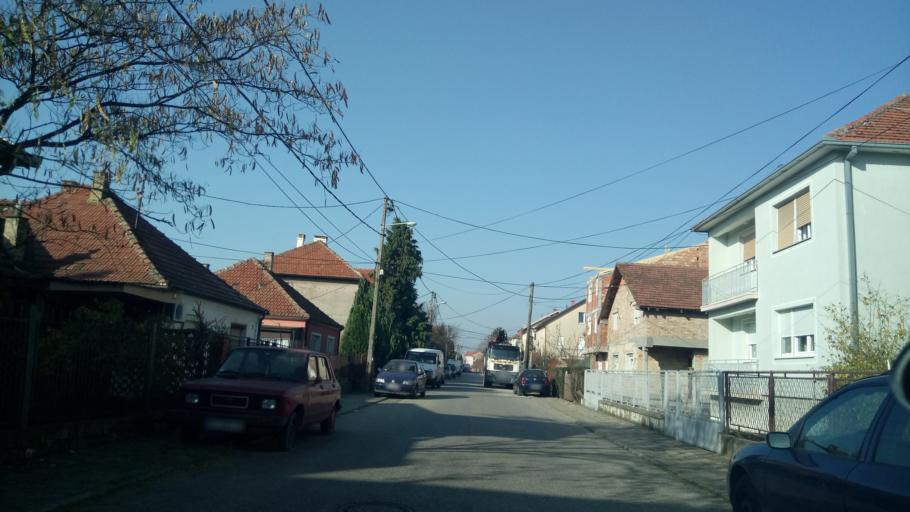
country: RS
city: Novi Banovci
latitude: 44.9007
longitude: 20.2930
